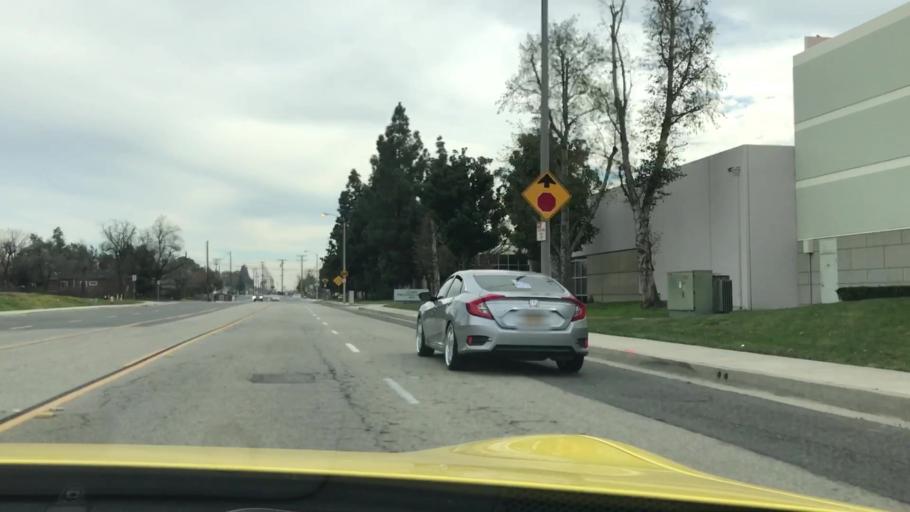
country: US
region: California
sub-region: San Bernardino County
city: Chino
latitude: 34.0117
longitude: -117.7004
